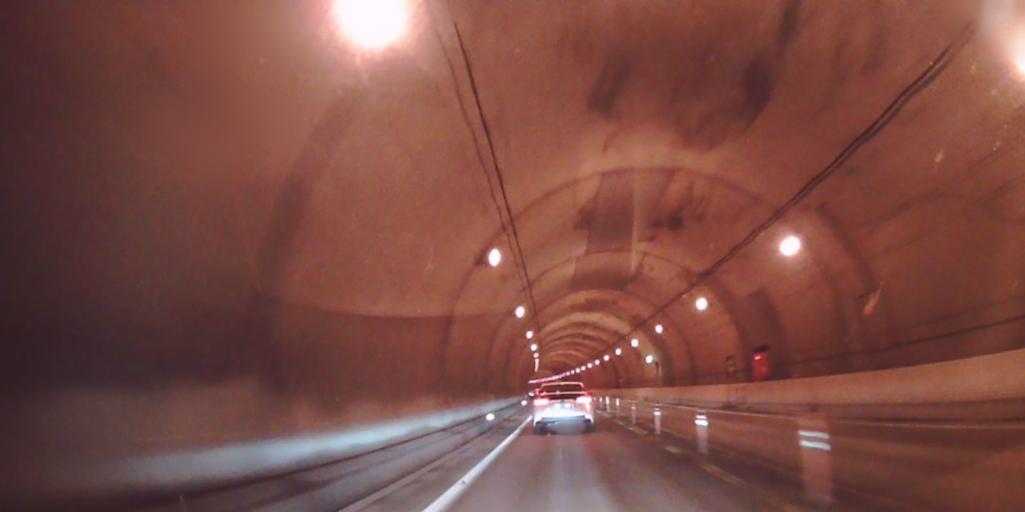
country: JP
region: Hokkaido
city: Date
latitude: 42.5540
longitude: 140.7853
